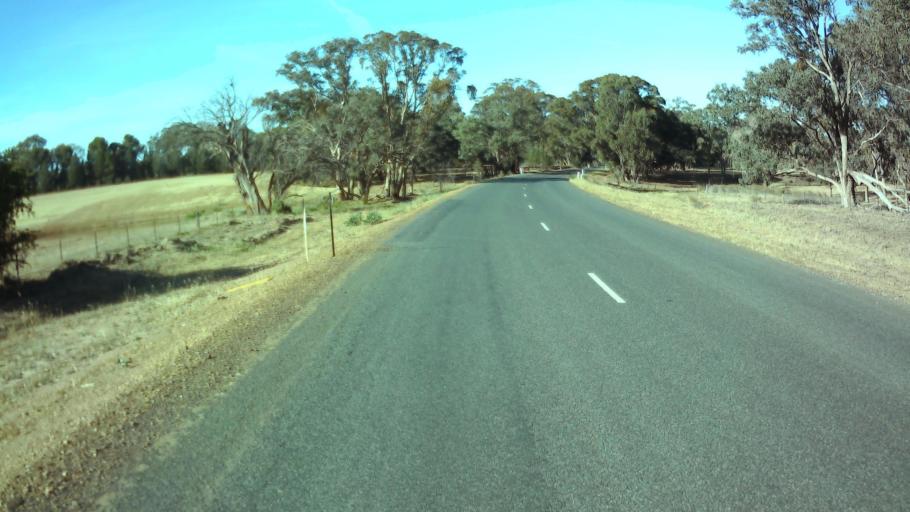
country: AU
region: New South Wales
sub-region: Weddin
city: Grenfell
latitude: -33.9883
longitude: 148.1398
